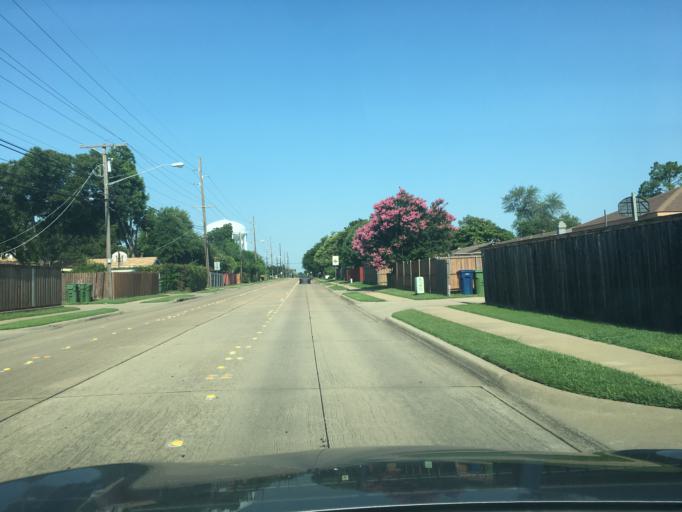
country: US
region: Texas
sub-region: Dallas County
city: Garland
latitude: 32.9239
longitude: -96.6859
